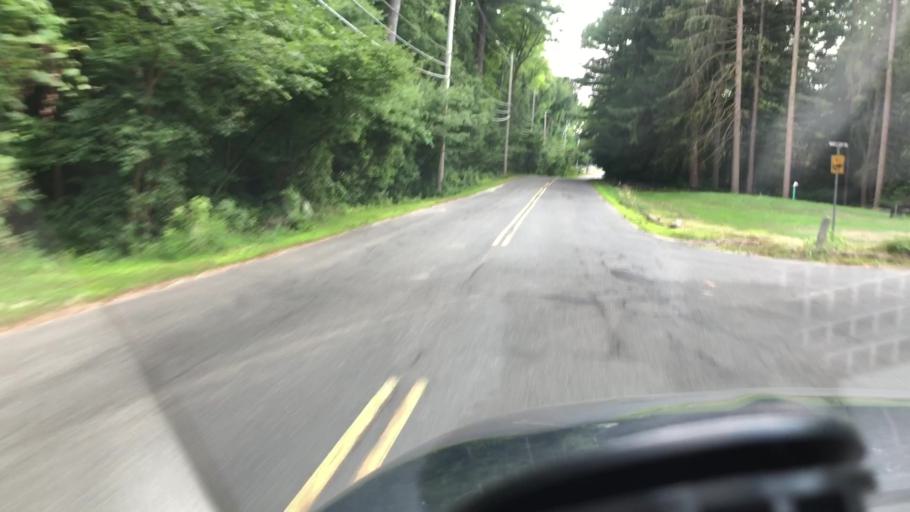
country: US
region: Massachusetts
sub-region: Hampden County
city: Holyoke
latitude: 42.1863
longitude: -72.6783
